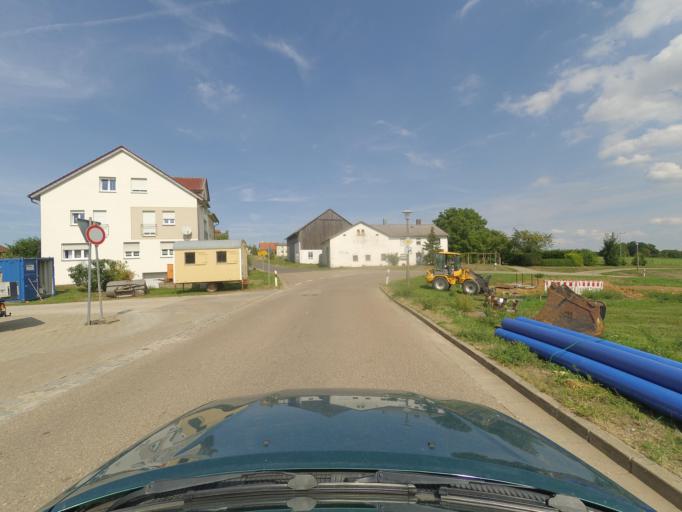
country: DE
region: Bavaria
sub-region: Regierungsbezirk Mittelfranken
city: Raitenbuch
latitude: 49.0072
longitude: 11.1806
